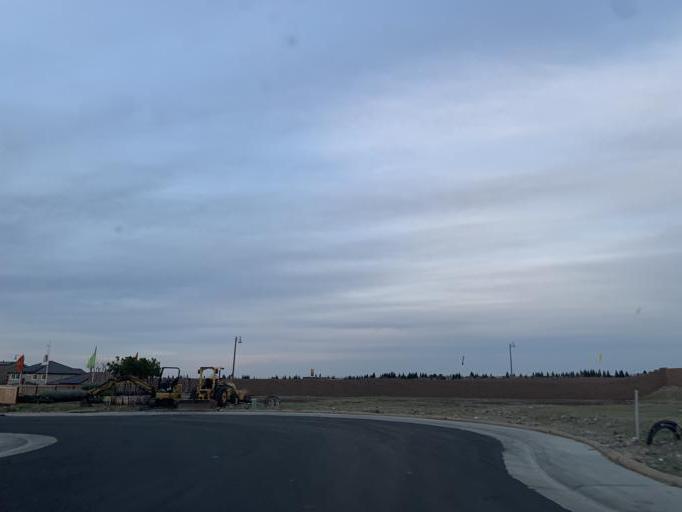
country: US
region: California
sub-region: Placer County
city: Lincoln
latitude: 38.8591
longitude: -121.2874
